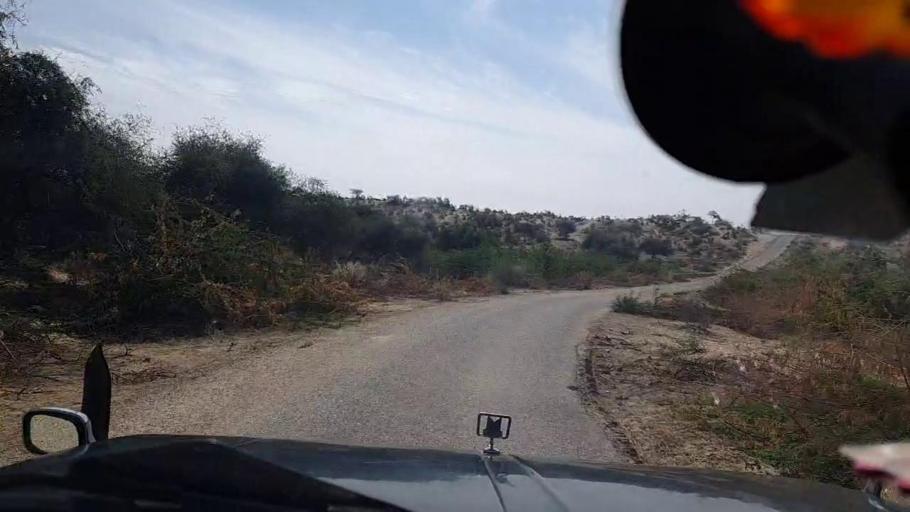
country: PK
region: Sindh
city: Diplo
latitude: 24.4043
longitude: 69.5877
